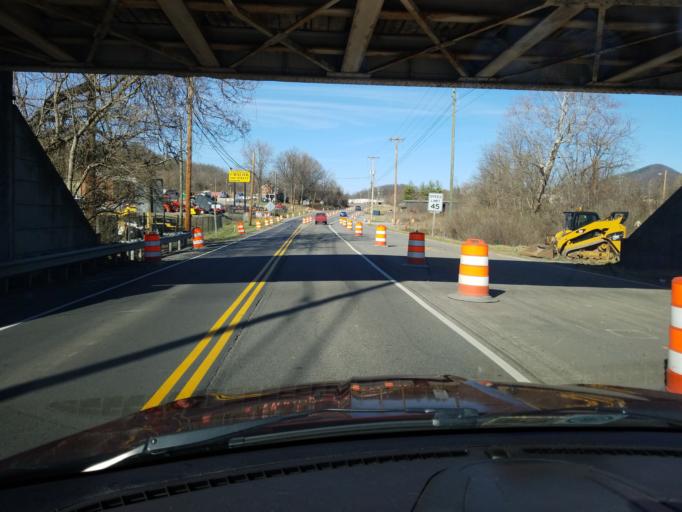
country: US
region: Virginia
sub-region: Botetourt County
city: Cloverdale
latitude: 37.3742
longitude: -79.9049
